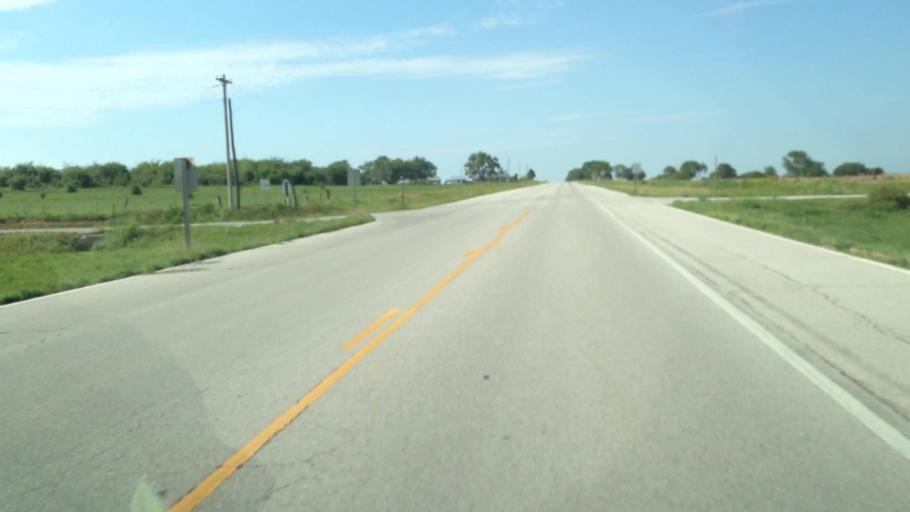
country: US
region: Kansas
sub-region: Neosho County
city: Erie
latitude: 37.4707
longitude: -95.2693
